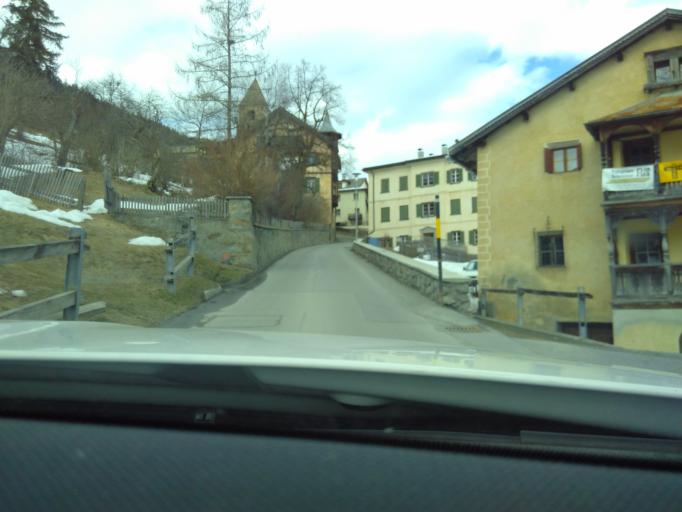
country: CH
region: Grisons
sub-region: Inn District
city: Scuol
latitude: 46.8333
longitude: 10.3810
